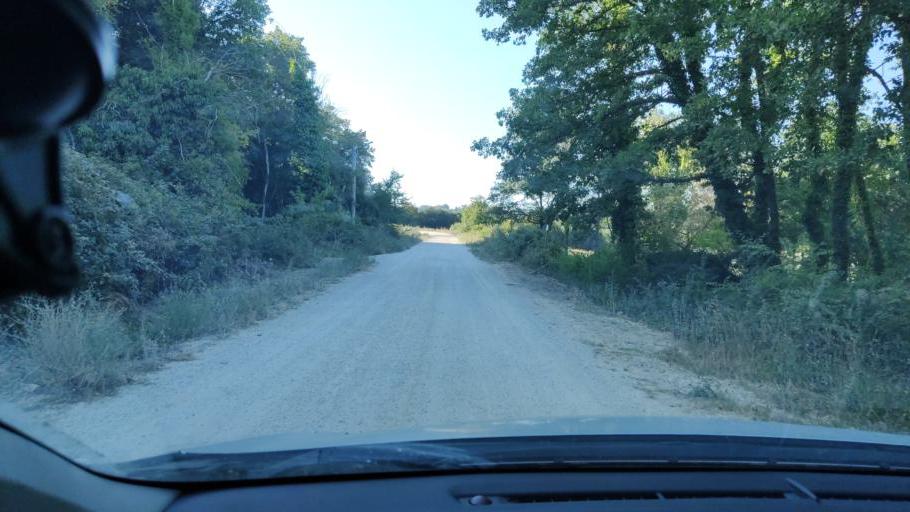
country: IT
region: Umbria
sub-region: Provincia di Terni
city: Amelia
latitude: 42.5416
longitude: 12.3840
